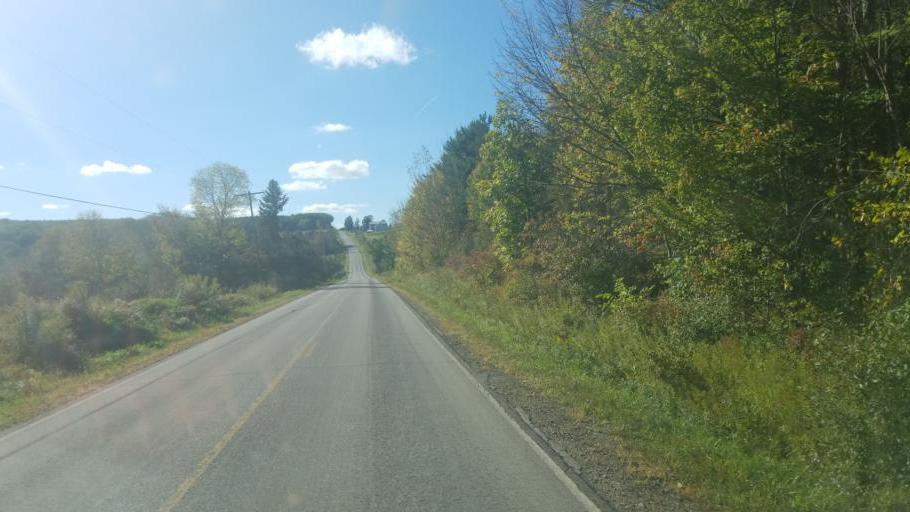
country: US
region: New York
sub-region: Allegany County
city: Friendship
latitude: 42.2768
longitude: -78.1602
